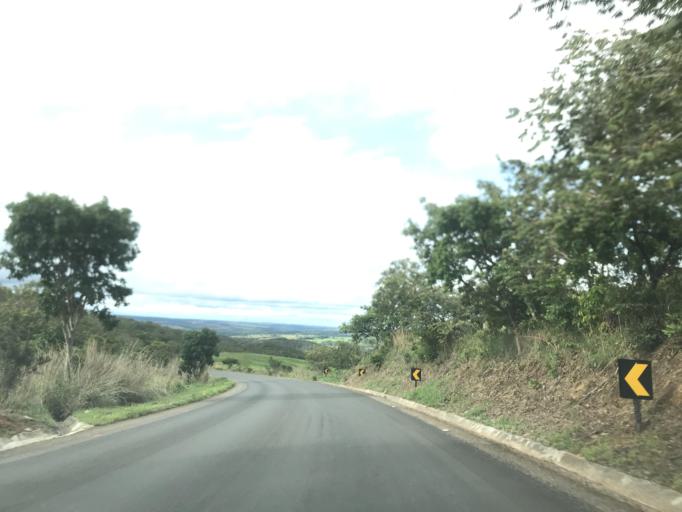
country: BR
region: Goias
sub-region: Vianopolis
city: Vianopolis
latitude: -16.9646
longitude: -48.5987
